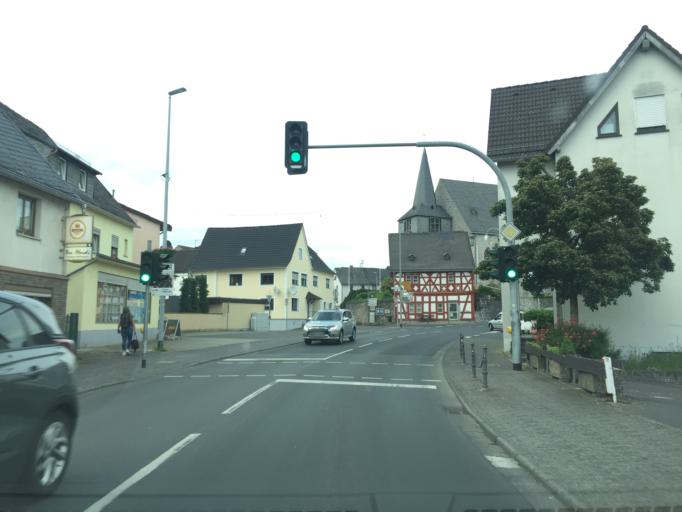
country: DE
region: Hesse
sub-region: Regierungsbezirk Giessen
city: Elz
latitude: 50.4350
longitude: 8.0342
